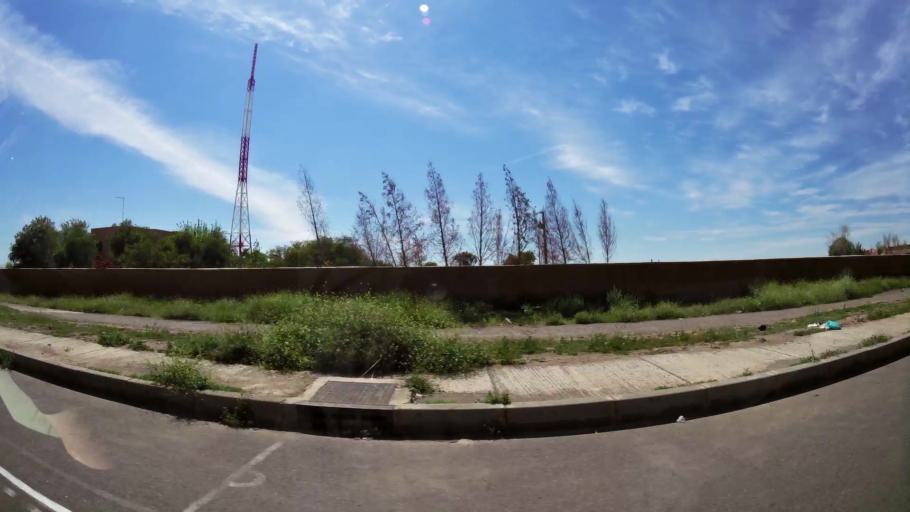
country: MA
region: Marrakech-Tensift-Al Haouz
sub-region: Marrakech
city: Marrakesh
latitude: 31.6313
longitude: -8.0755
